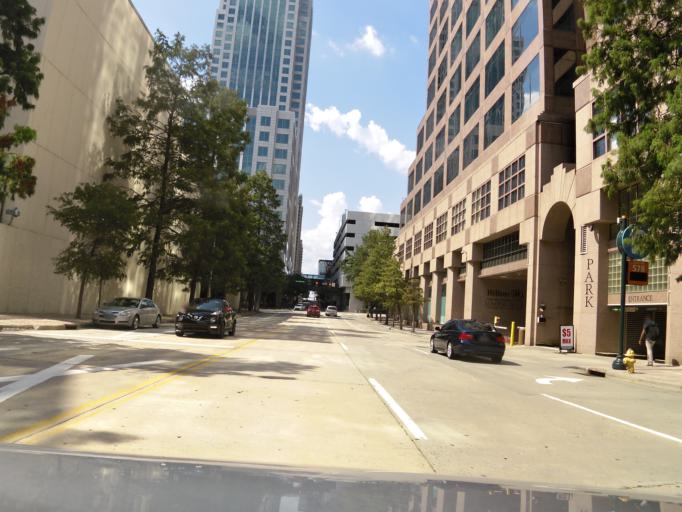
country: US
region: North Carolina
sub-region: Mecklenburg County
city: Charlotte
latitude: 35.2234
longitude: -80.8445
